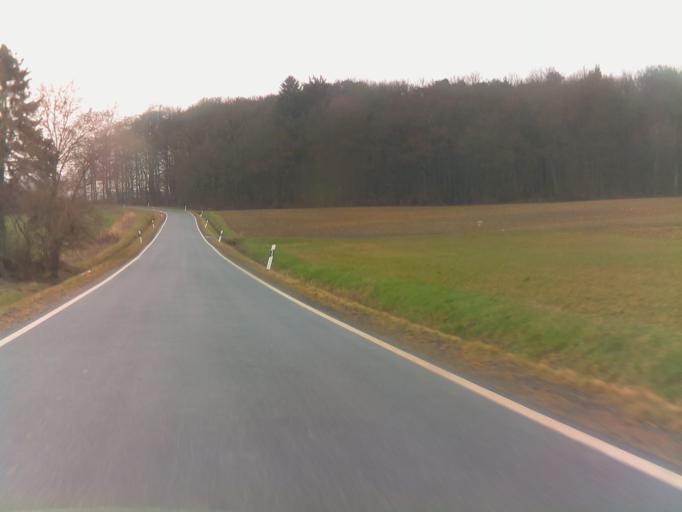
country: DE
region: Rheinland-Pfalz
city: Gosenroth
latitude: 49.8971
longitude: 7.3290
